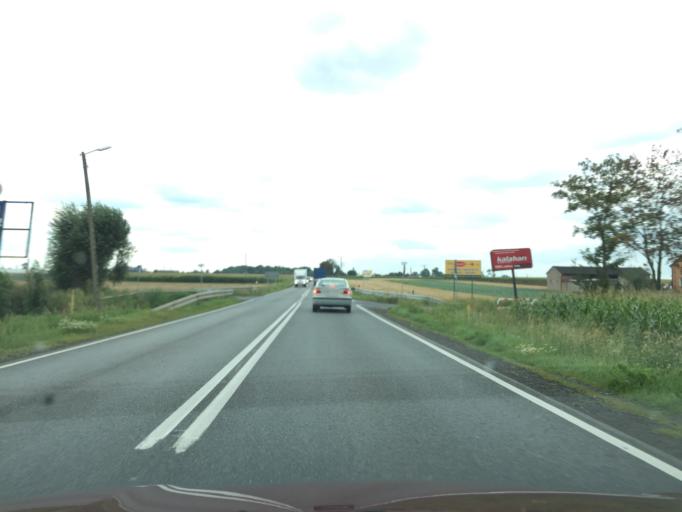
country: PL
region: Greater Poland Voivodeship
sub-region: Kalisz
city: Kalisz
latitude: 51.8243
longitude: 18.0940
